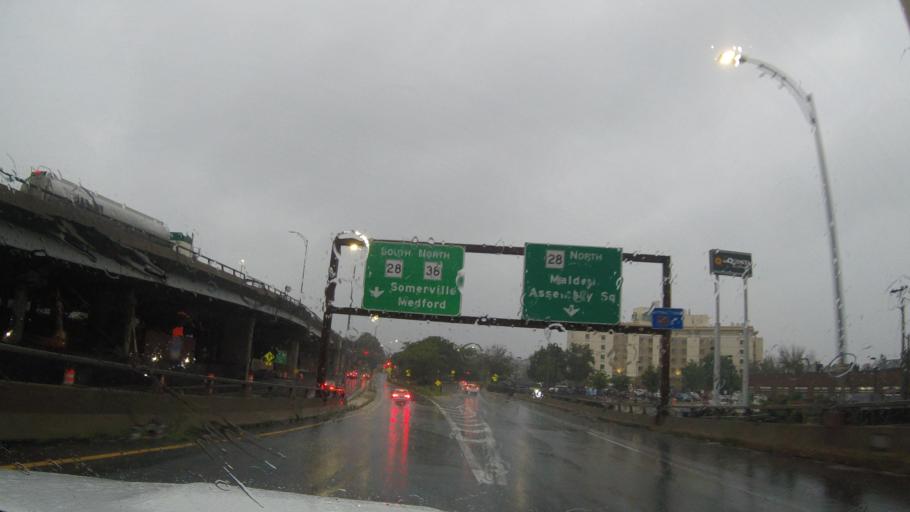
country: US
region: Massachusetts
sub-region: Middlesex County
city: Somerville
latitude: 42.3930
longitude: -71.0842
